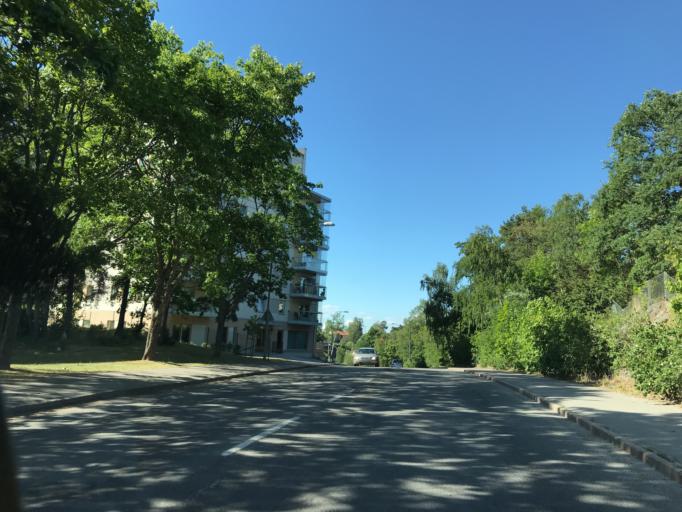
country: SE
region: Stockholm
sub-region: Huddinge Kommun
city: Segeltorp
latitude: 59.2977
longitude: 17.9424
